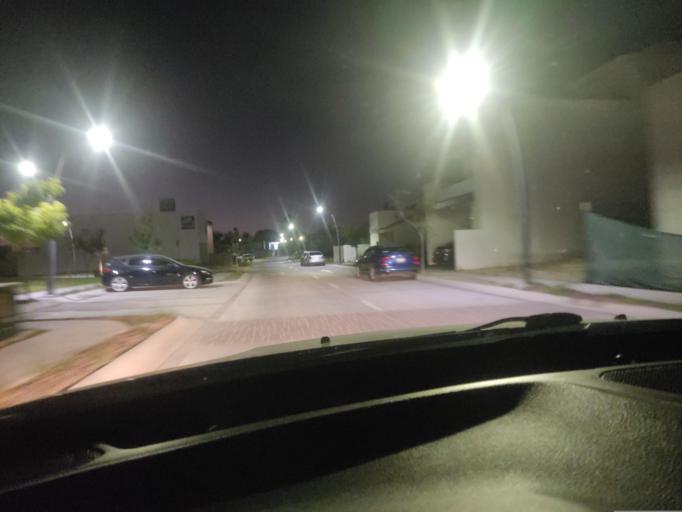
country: MX
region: Guanajuato
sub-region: Leon
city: Ladrilleras del Refugio
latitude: 21.0857
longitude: -101.5606
